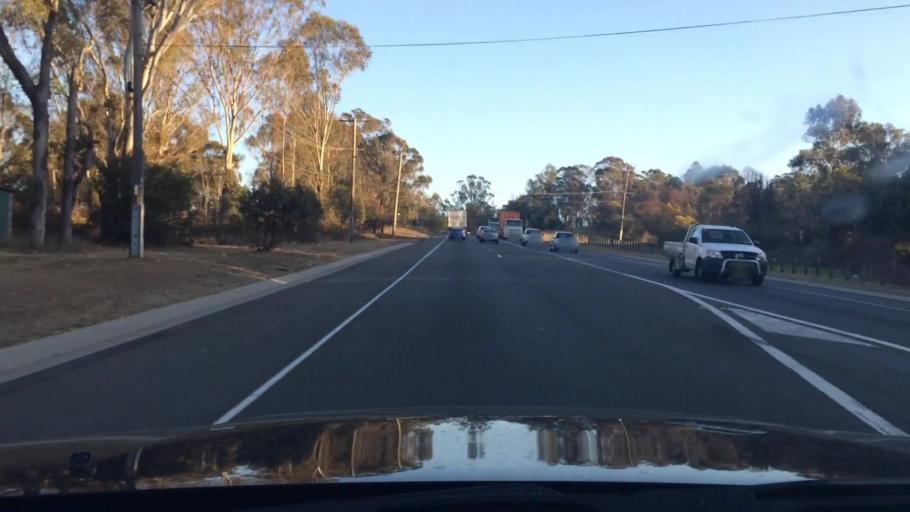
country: AU
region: New South Wales
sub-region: Fairfield
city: Carramar
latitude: -33.8950
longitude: 150.9718
